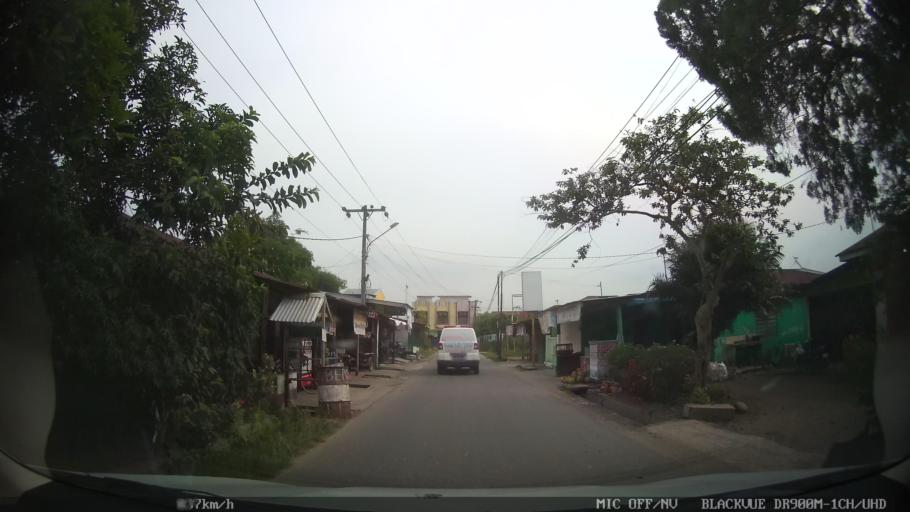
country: ID
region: North Sumatra
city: Medan
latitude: 3.5706
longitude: 98.7566
